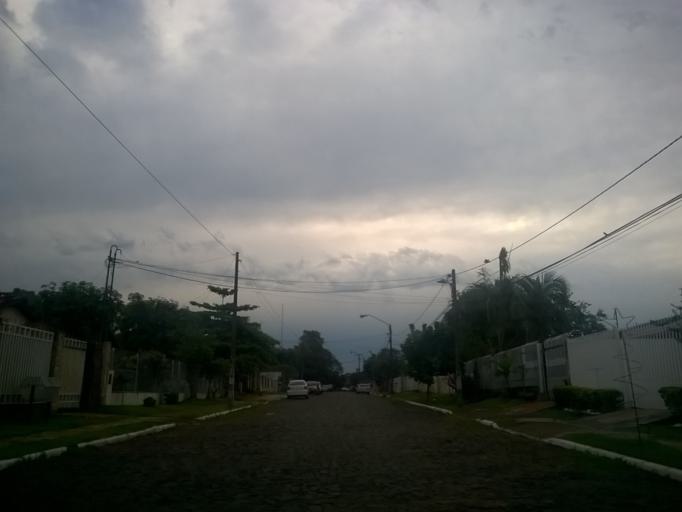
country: PY
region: Alto Parana
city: Presidente Franco
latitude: -25.5349
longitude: -54.6279
